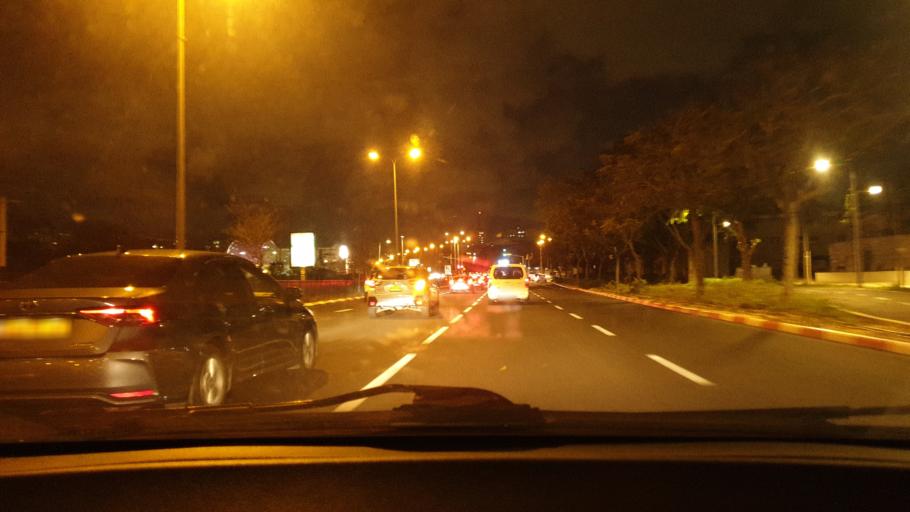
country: IL
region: Central District
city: Rishon LeZiyyon
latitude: 31.9521
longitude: 34.8027
